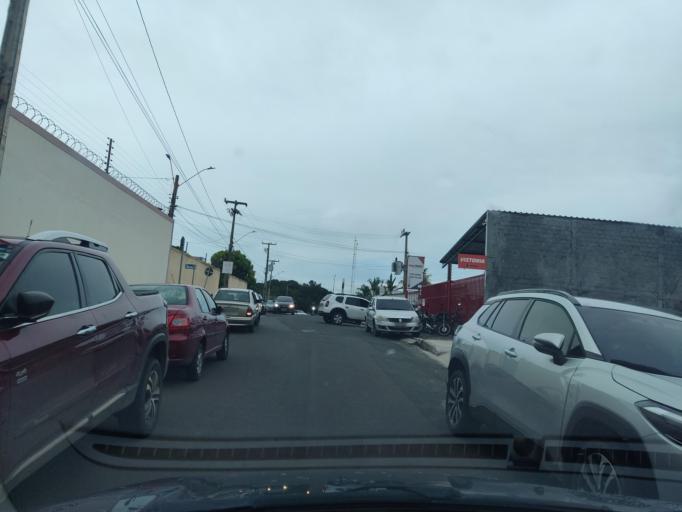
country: BR
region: Piaui
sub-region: Teresina
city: Teresina
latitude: -5.0775
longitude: -42.7537
